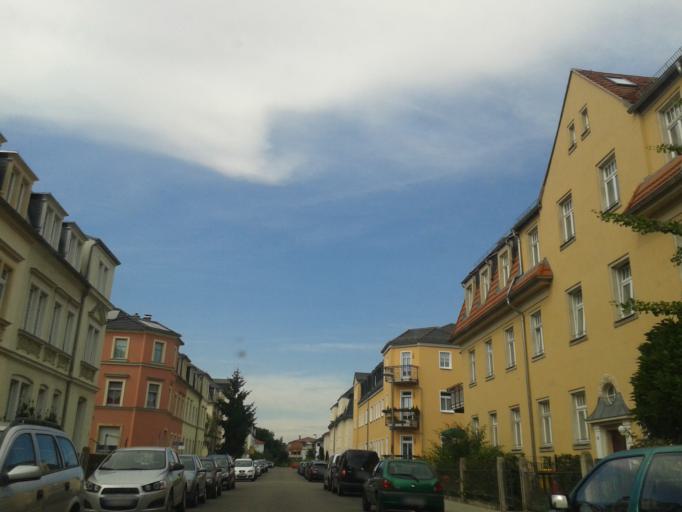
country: DE
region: Saxony
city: Dresden
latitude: 51.0715
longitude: 13.6952
